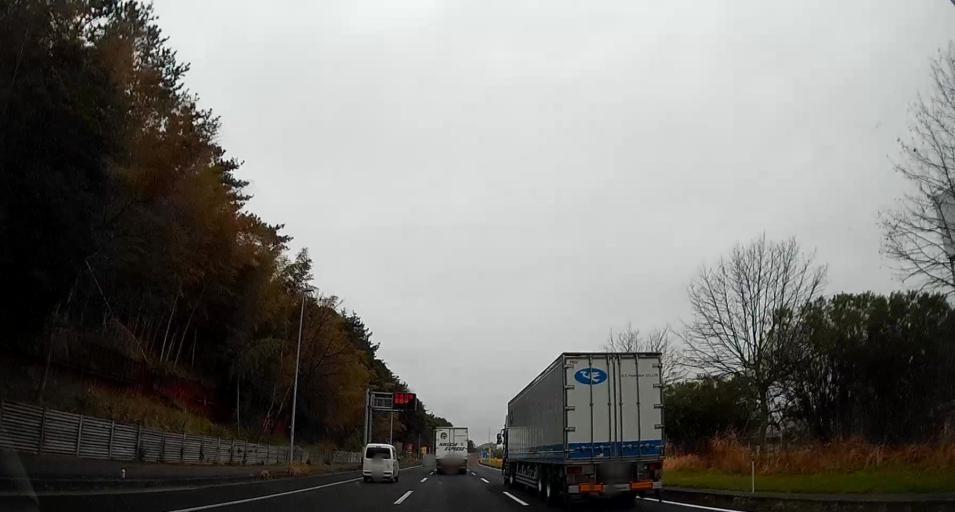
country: JP
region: Chiba
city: Chiba
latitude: 35.6319
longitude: 140.0852
